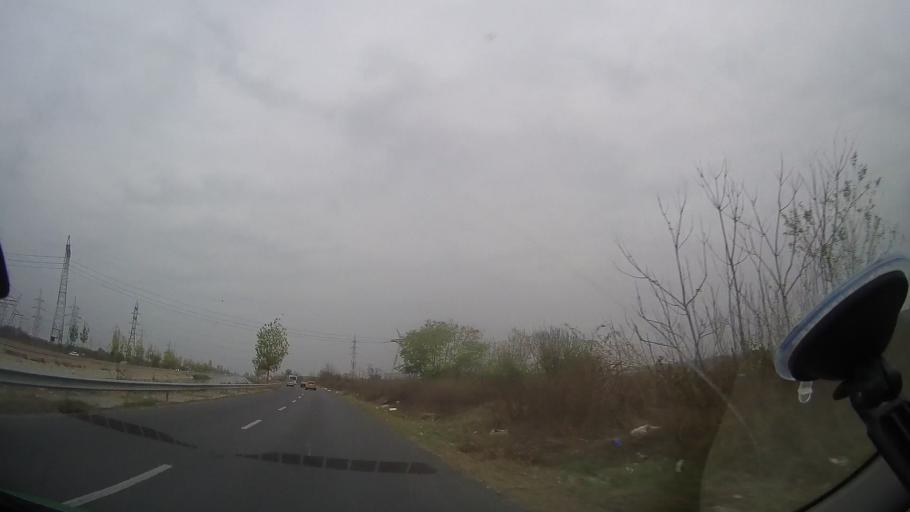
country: RO
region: Ilfov
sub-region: Comuna Popesti-Leordeni
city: Popesti-Leordeni
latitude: 44.3939
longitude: 26.1806
